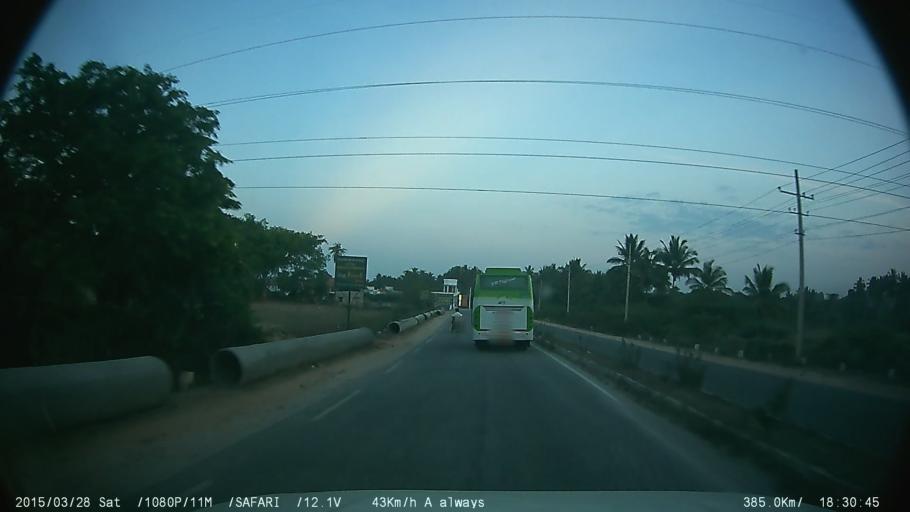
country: IN
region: Karnataka
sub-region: Mandya
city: Shrirangapattana
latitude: 12.3947
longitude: 76.5843
